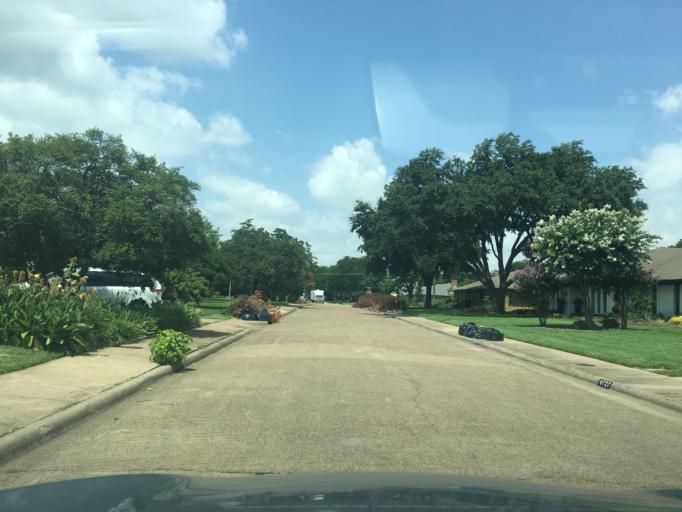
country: US
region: Texas
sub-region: Dallas County
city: Addison
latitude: 32.9233
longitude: -96.8279
